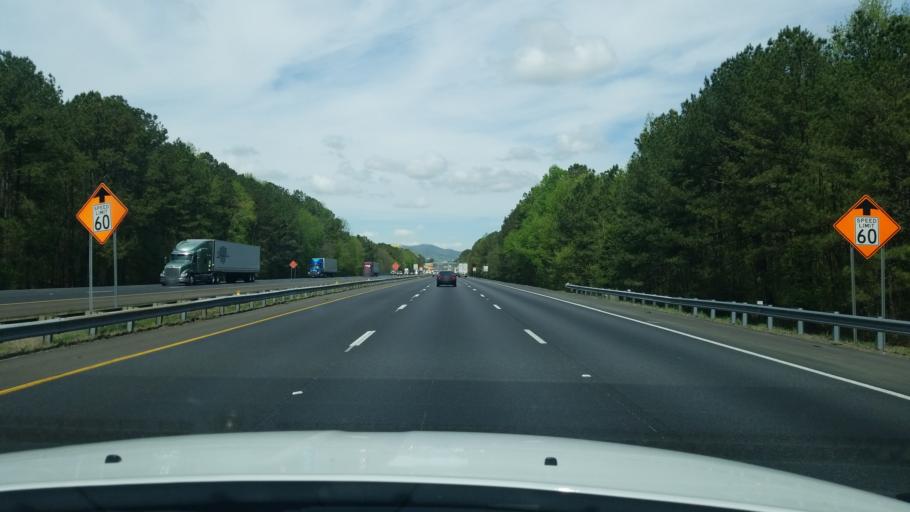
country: US
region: Georgia
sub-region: Whitfield County
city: Dalton
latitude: 34.6374
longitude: -84.9776
